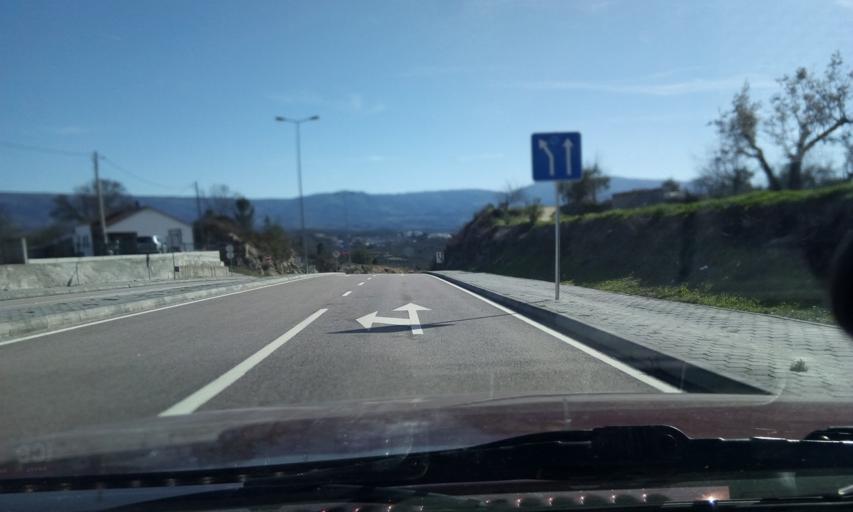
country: PT
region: Guarda
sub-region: Fornos de Algodres
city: Fornos de Algodres
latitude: 40.6152
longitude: -7.5383
